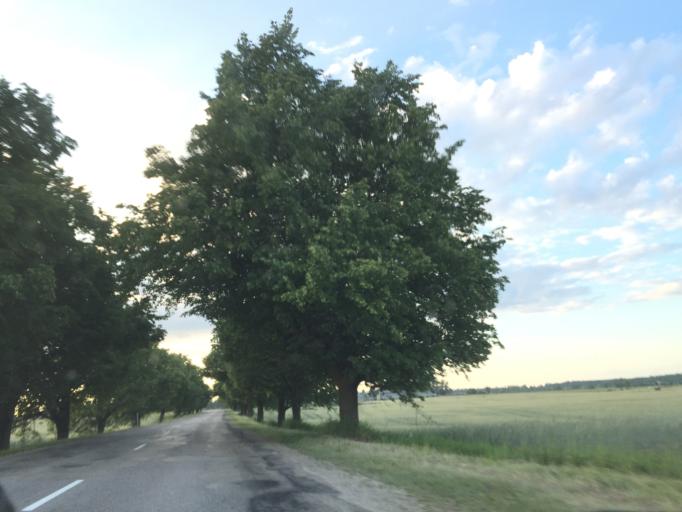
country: LV
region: Sigulda
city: Sigulda
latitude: 57.1335
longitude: 24.8960
